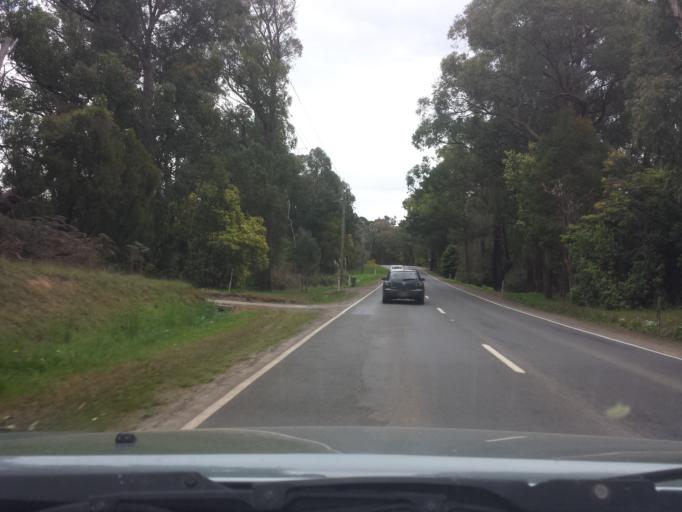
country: AU
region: Victoria
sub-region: Yarra Ranges
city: Mount Evelyn
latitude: -37.7999
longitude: 145.3959
